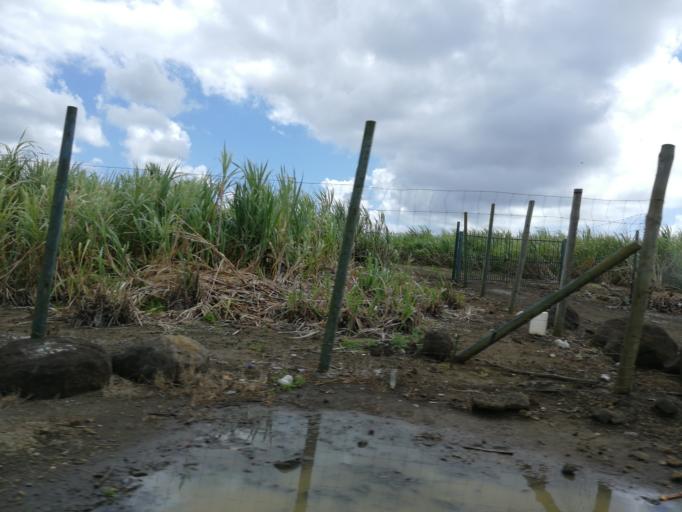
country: MU
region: Riviere du Rempart
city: Esperance Trebuchet
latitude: -20.0727
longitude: 57.6644
